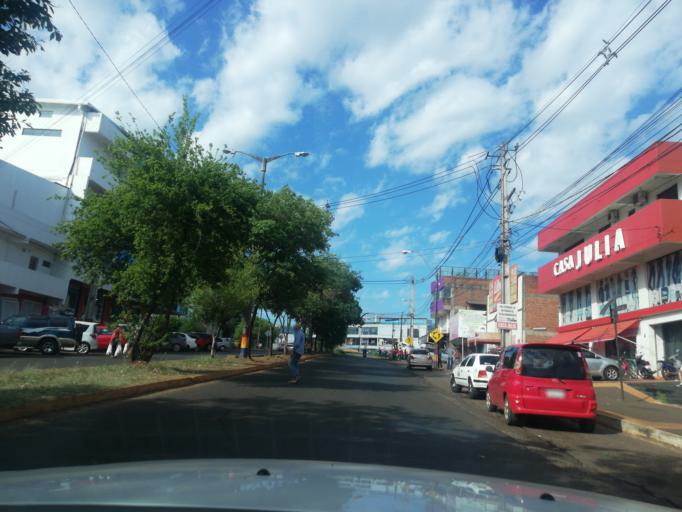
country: PY
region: Itapua
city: Encarnacion
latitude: -27.3572
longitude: -55.8492
